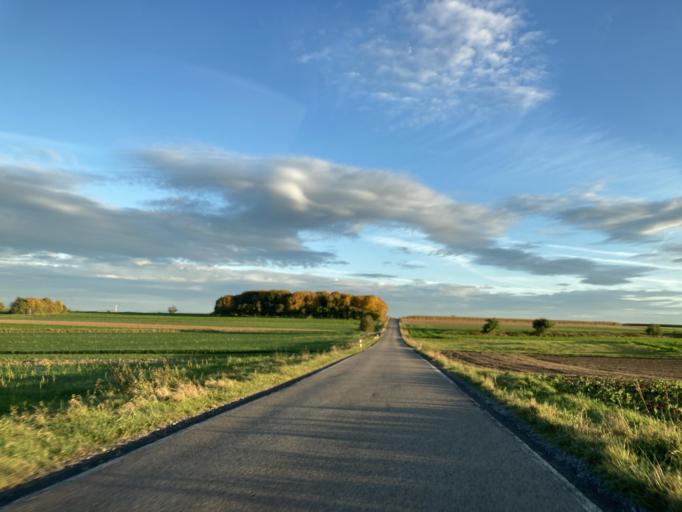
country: DE
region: Baden-Wuerttemberg
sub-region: Regierungsbezirk Stuttgart
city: Motzingen
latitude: 48.4932
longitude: 8.7789
